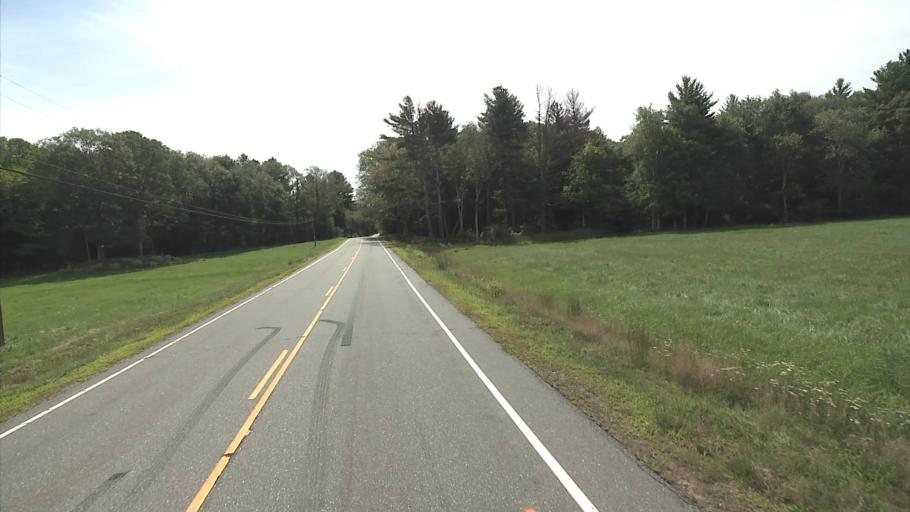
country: US
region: Massachusetts
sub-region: Hampden County
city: Holland
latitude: 41.9383
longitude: -72.0988
